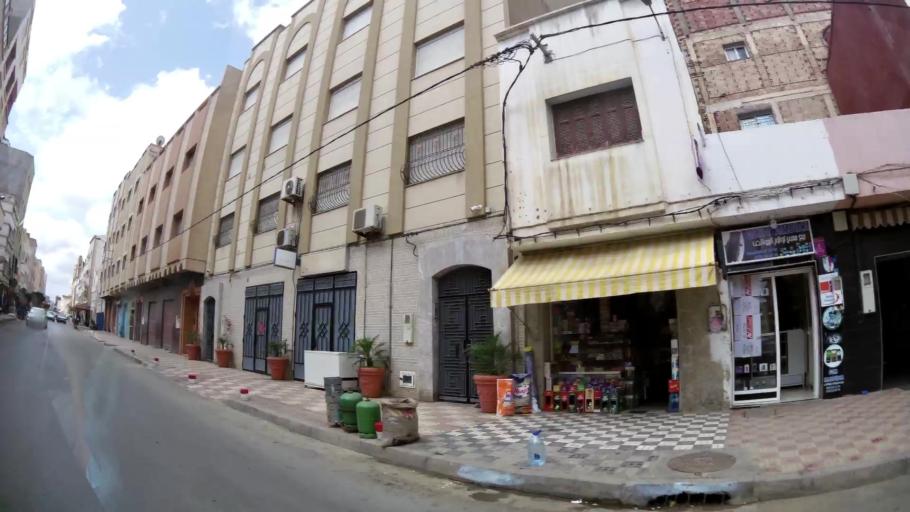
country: MA
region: Oriental
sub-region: Nador
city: Nador
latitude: 35.1667
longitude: -2.9311
